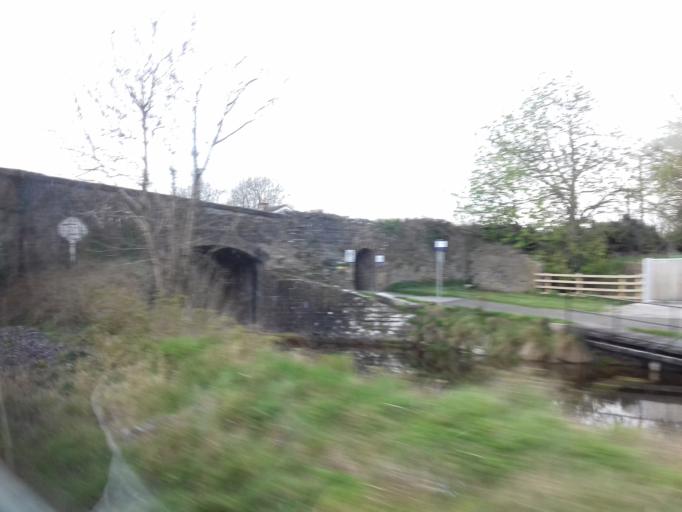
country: IE
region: Leinster
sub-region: Kildare
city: Maynooth
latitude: 53.3809
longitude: -6.6209
